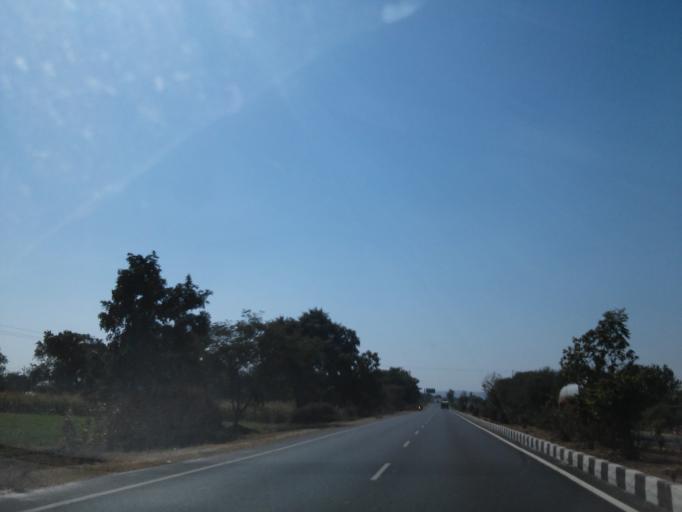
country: IN
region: Gujarat
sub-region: Sabar Kantha
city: Modasa
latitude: 23.6306
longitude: 73.3005
